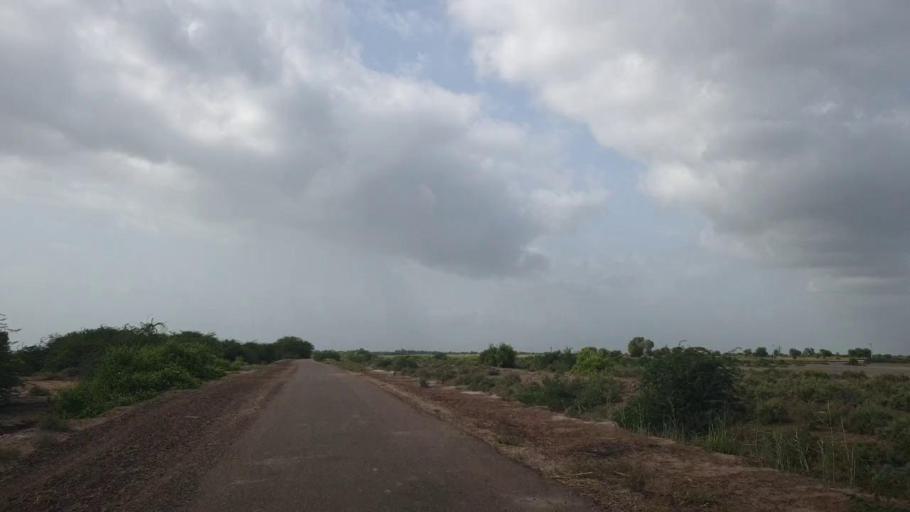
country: PK
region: Sindh
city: Kadhan
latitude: 24.5600
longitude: 69.0638
